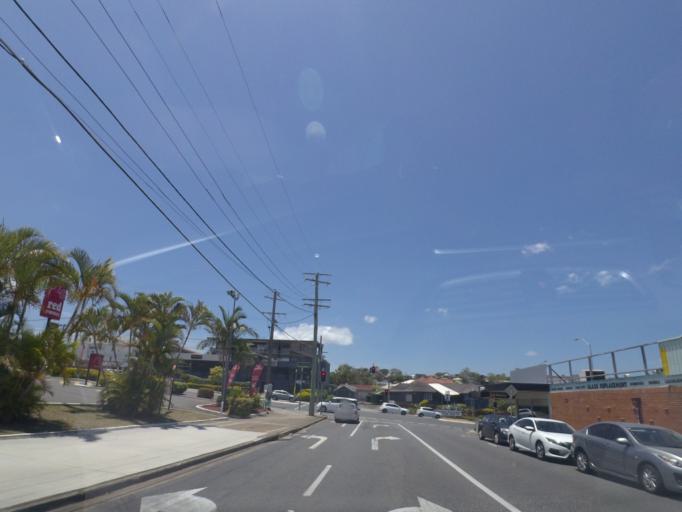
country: AU
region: Queensland
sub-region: Brisbane
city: Mount Gravatt East
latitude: -27.5370
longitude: 153.0776
